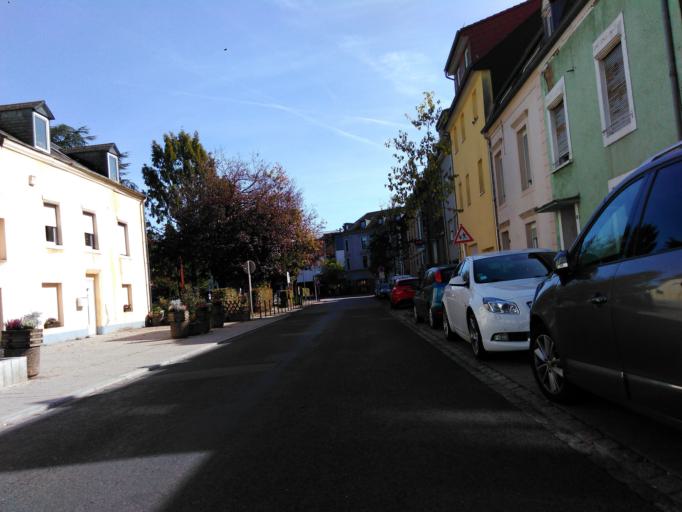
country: LU
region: Luxembourg
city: Tetange
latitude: 49.4739
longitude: 6.0371
